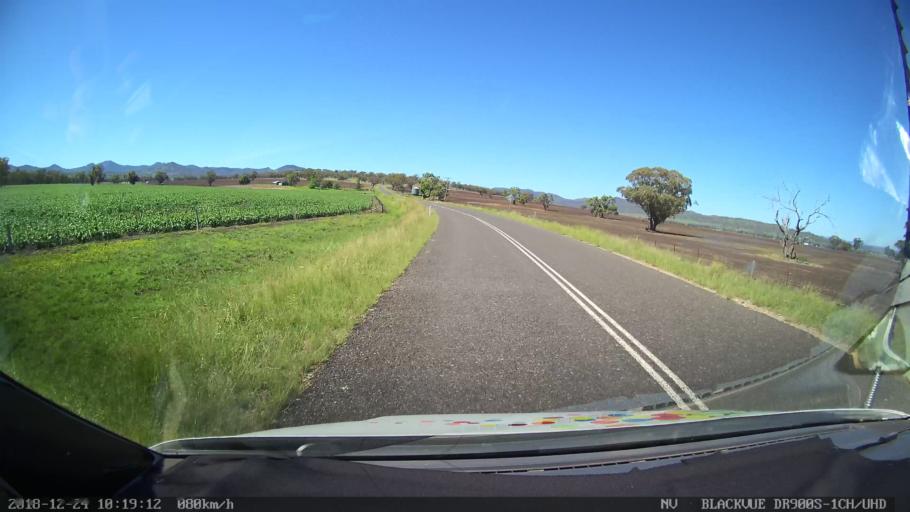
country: AU
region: New South Wales
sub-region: Liverpool Plains
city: Quirindi
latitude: -31.7273
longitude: 150.5660
